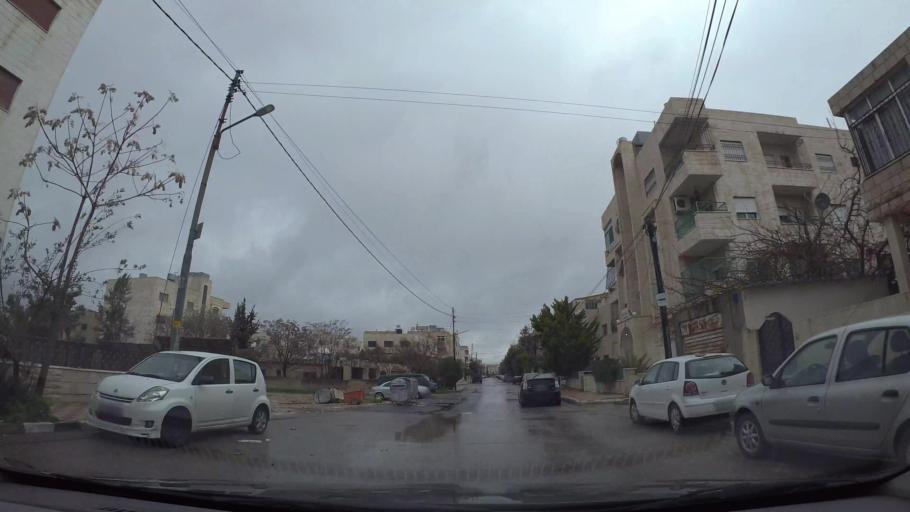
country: JO
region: Amman
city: Wadi as Sir
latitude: 31.9635
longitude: 35.8617
